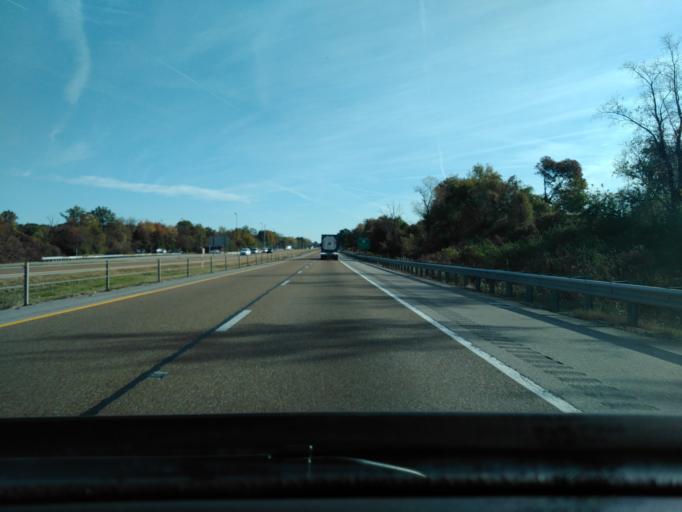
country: US
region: Illinois
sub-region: Madison County
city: Collinsville
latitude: 38.7028
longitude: -89.9827
